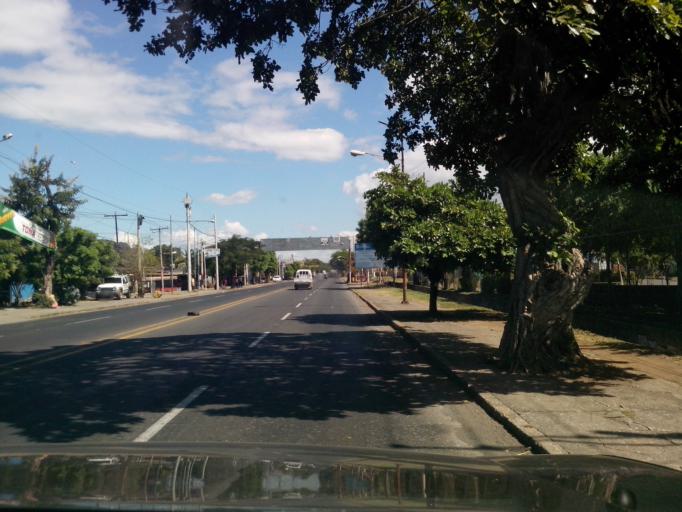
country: NI
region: Managua
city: Ciudad Sandino
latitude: 12.1381
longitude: -86.3056
